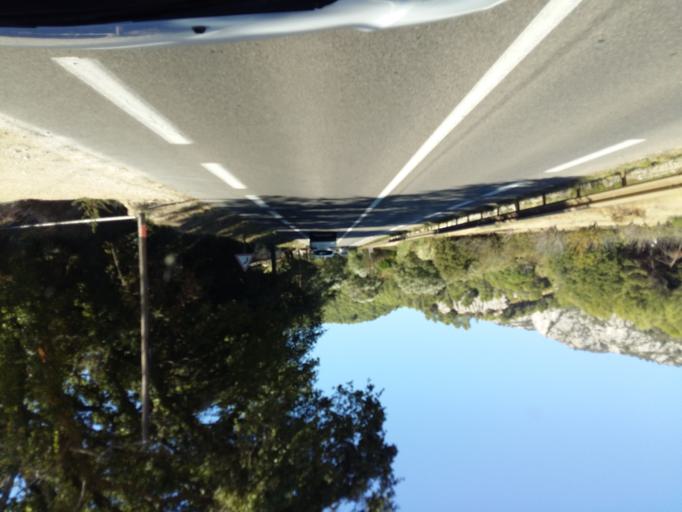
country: FR
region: Provence-Alpes-Cote d'Azur
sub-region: Departement des Bouches-du-Rhone
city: Mallemort
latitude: 43.7563
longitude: 5.1546
